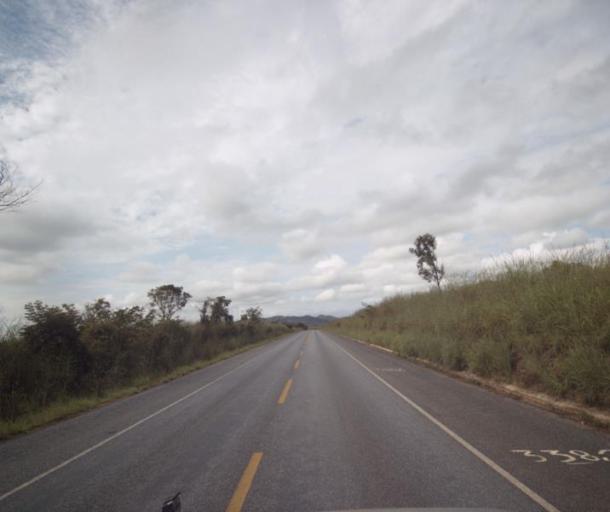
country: BR
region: Goias
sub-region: Pirenopolis
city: Pirenopolis
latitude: -15.5481
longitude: -48.6228
